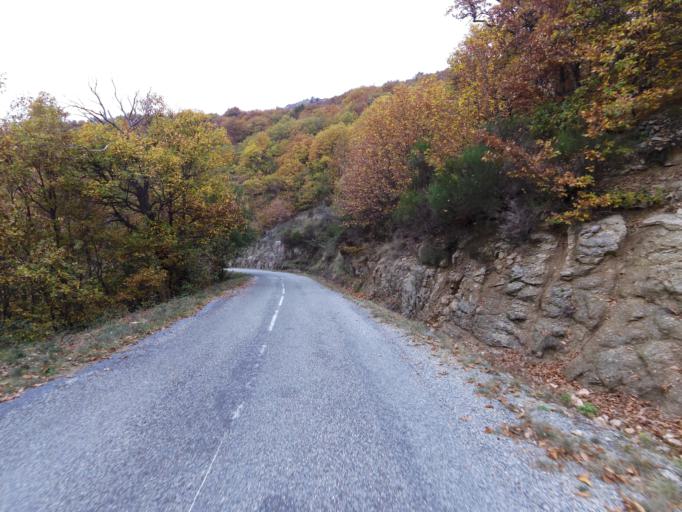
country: FR
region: Rhone-Alpes
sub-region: Departement de l'Ardeche
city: Les Vans
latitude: 44.5061
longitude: 4.0424
